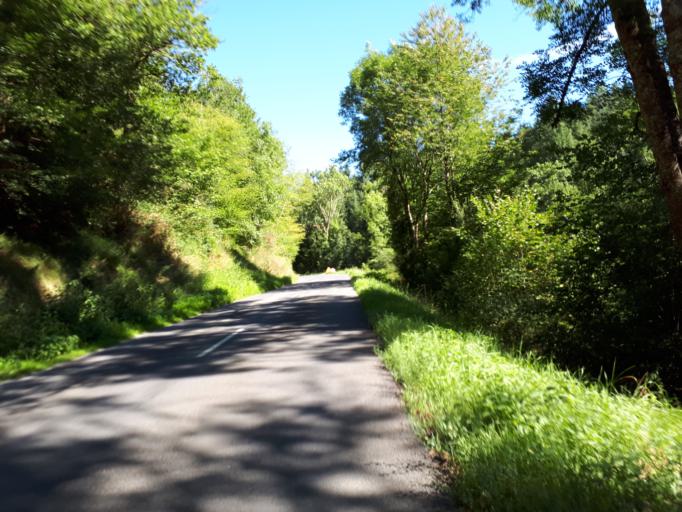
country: FR
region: Rhone-Alpes
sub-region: Departement de la Loire
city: Pouilly-les-Feurs
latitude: 45.8097
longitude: 4.2476
